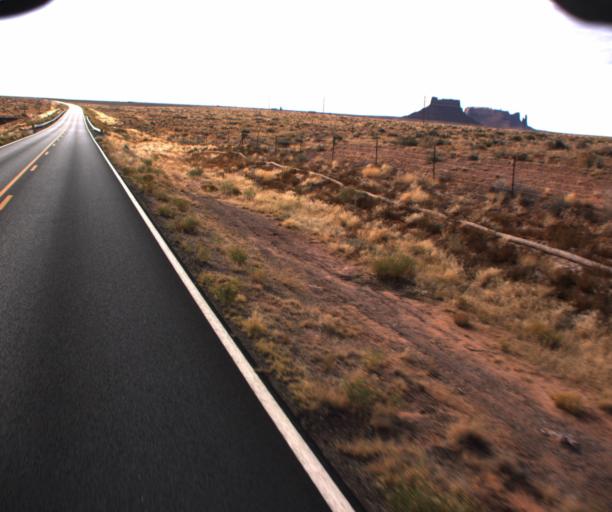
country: US
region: Arizona
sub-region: Apache County
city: Many Farms
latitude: 36.5673
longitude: -109.5450
